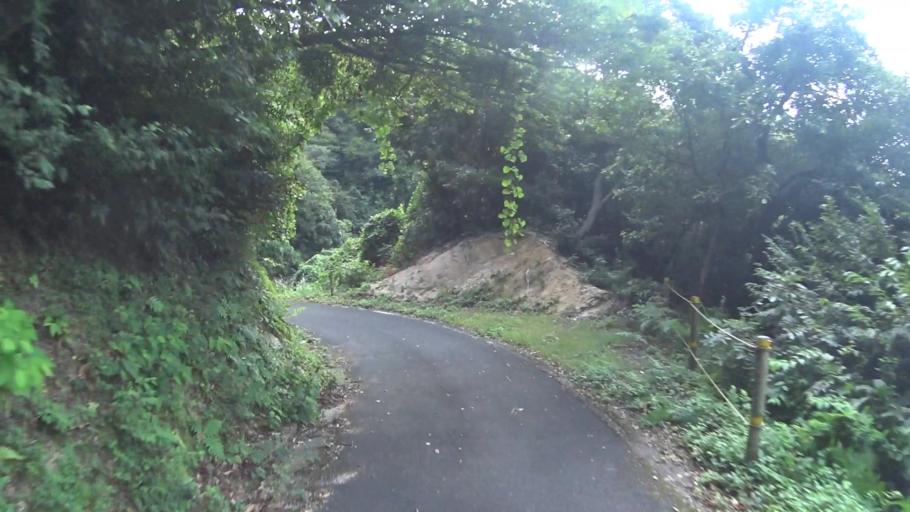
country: JP
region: Kyoto
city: Miyazu
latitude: 35.6646
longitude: 135.1346
